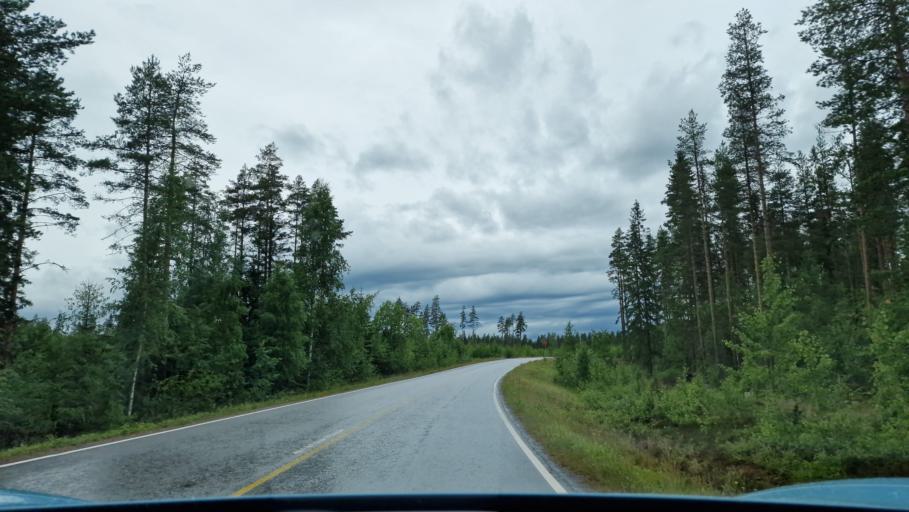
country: FI
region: Central Finland
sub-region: Saarijaervi-Viitasaari
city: Pylkoenmaeki
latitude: 62.6698
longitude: 24.5184
